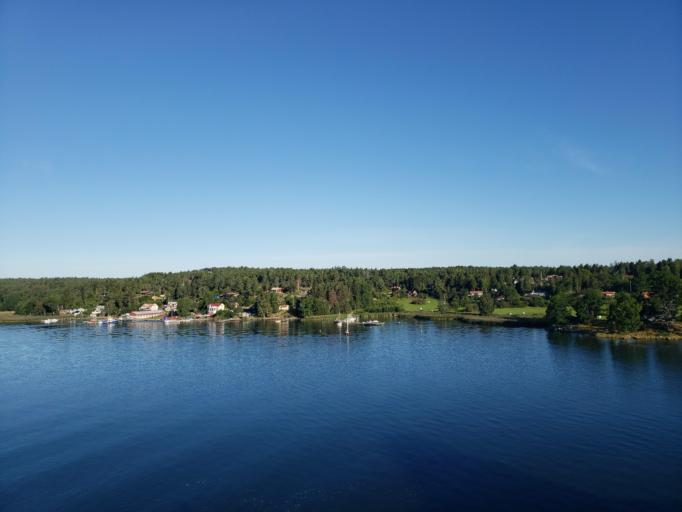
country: SE
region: Stockholm
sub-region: Vaxholms Kommun
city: Vaxholm
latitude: 59.5016
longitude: 18.4710
